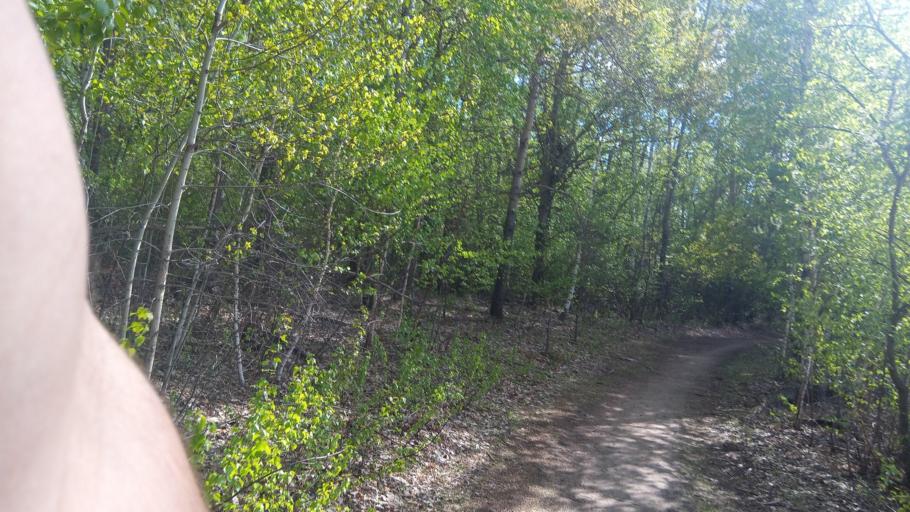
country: RU
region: Chelyabinsk
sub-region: Gorod Chelyabinsk
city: Chelyabinsk
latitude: 55.1672
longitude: 61.3206
